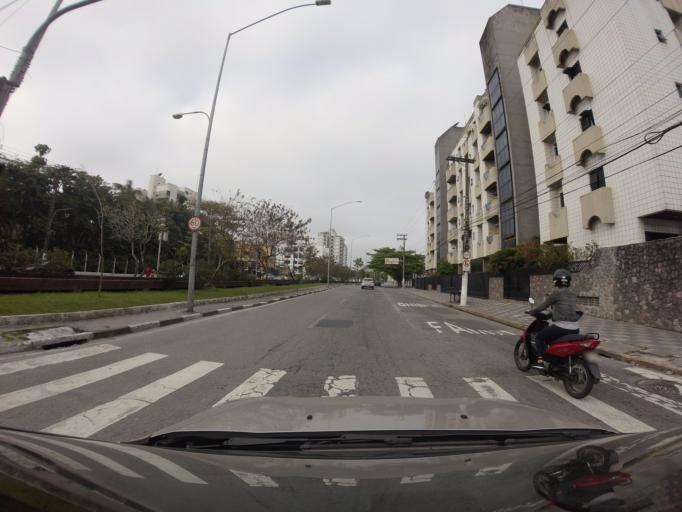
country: BR
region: Sao Paulo
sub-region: Guaruja
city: Guaruja
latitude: -23.9884
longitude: -46.2470
